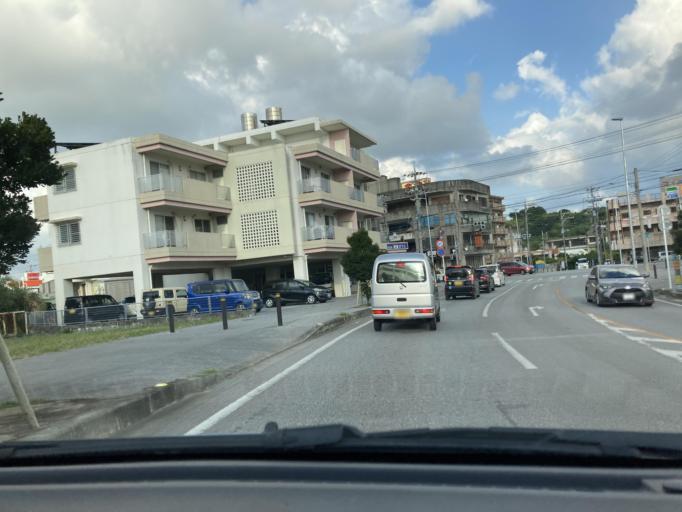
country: JP
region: Okinawa
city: Itoman
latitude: 26.1345
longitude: 127.6862
